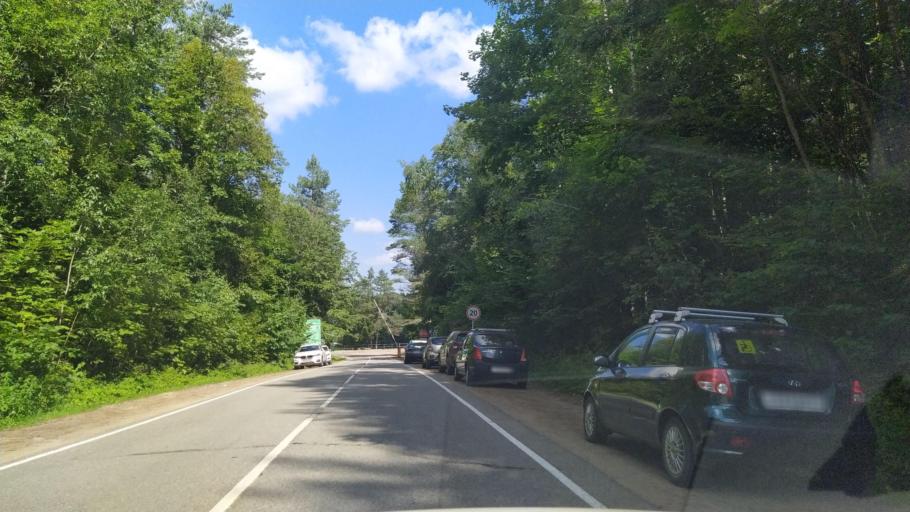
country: RU
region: Pskov
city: Pushkinskiye Gory
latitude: 57.0740
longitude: 28.9562
